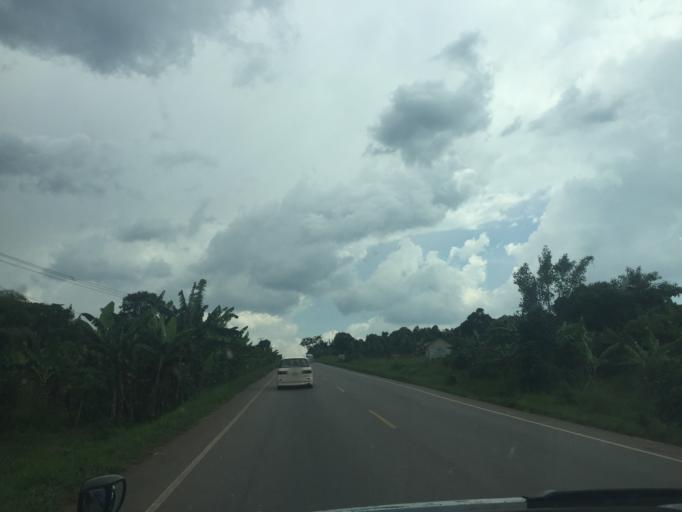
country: UG
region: Central Region
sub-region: Luwero District
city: Wobulenzi
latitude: 0.6517
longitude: 32.5309
